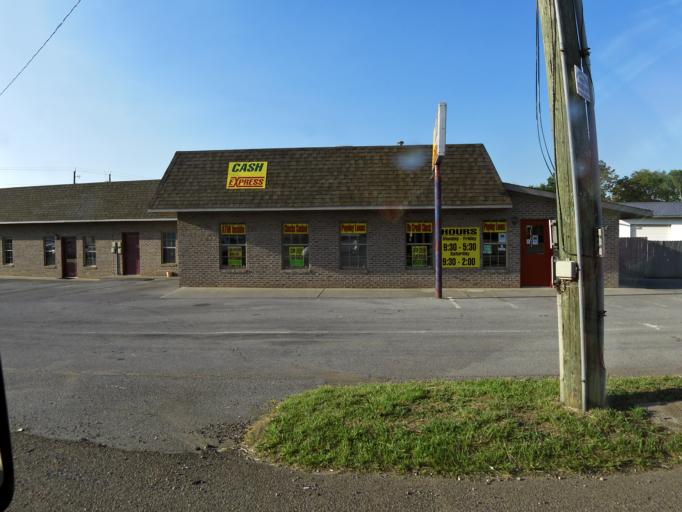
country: US
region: Tennessee
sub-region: Sevier County
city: Seymour
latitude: 35.8787
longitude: -83.7741
